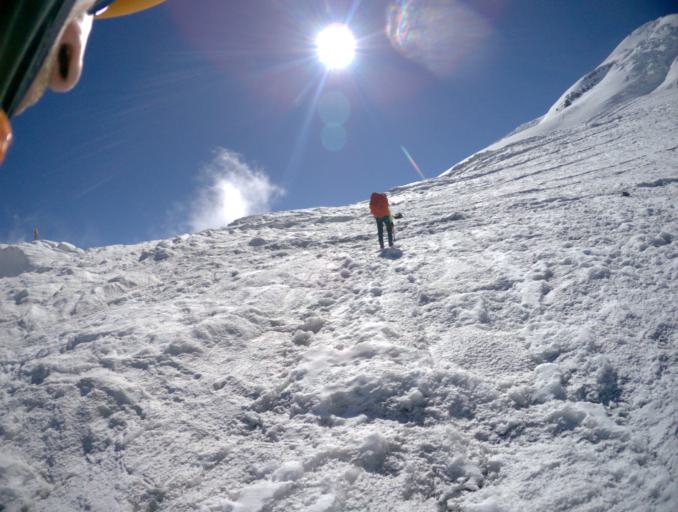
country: RU
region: Kabardino-Balkariya
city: Terskol
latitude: 43.3856
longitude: 42.4373
